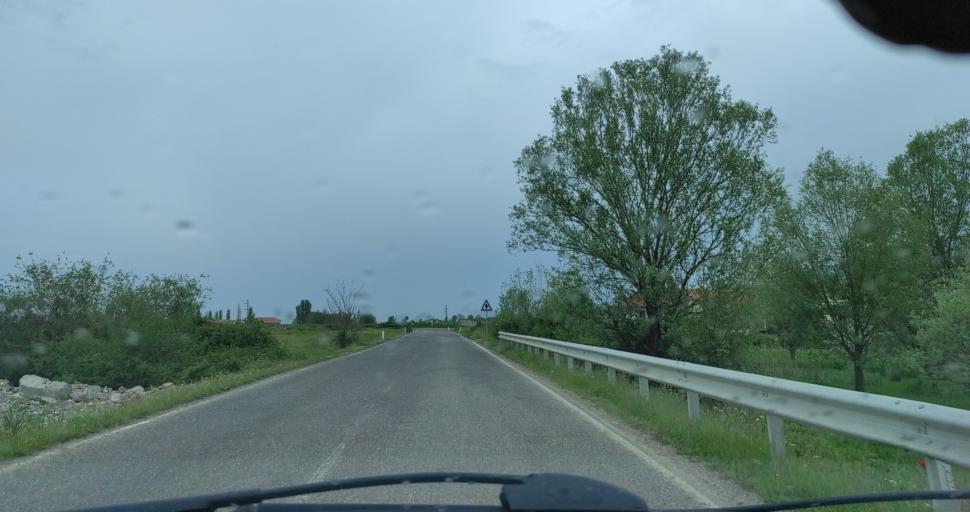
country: AL
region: Lezhe
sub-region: Rrethi i Kurbinit
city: Mamurras
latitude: 41.5937
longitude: 19.6988
